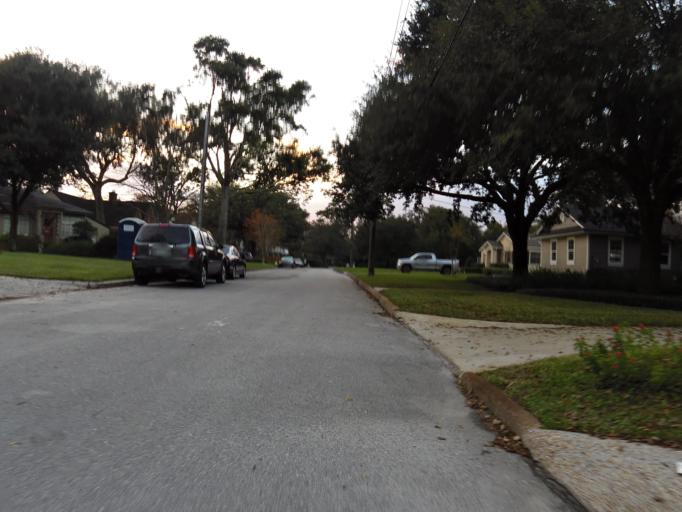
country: US
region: Florida
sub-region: Duval County
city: Jacksonville
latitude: 30.2859
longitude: -81.6538
